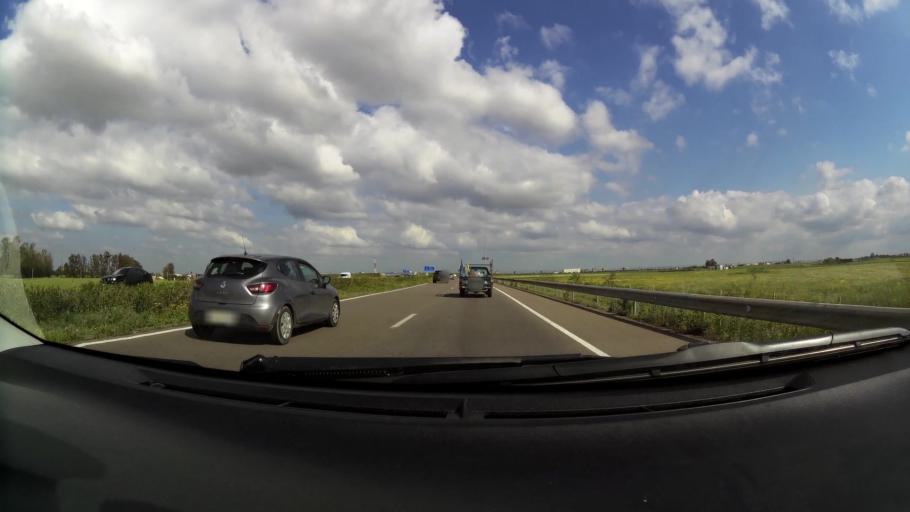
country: MA
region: Chaouia-Ouardigha
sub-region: Settat Province
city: Berrechid
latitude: 33.3044
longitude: -7.5817
